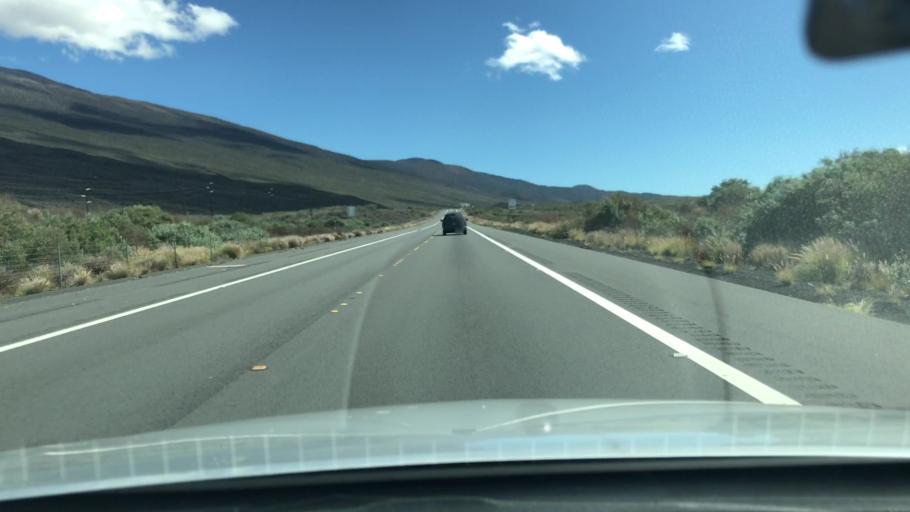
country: US
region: Hawaii
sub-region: Hawaii County
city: Waimea
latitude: 19.7653
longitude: -155.5673
